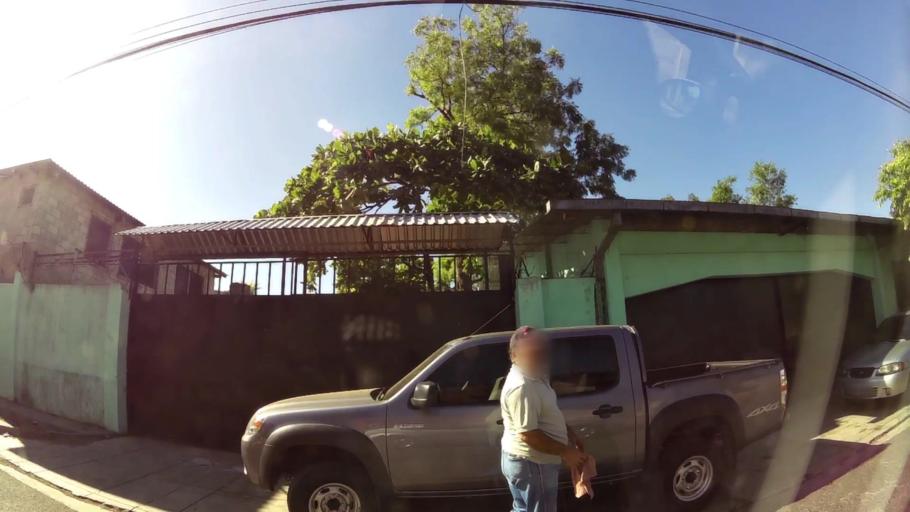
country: SV
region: Sonsonate
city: Sonzacate
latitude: 13.7364
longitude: -89.7159
